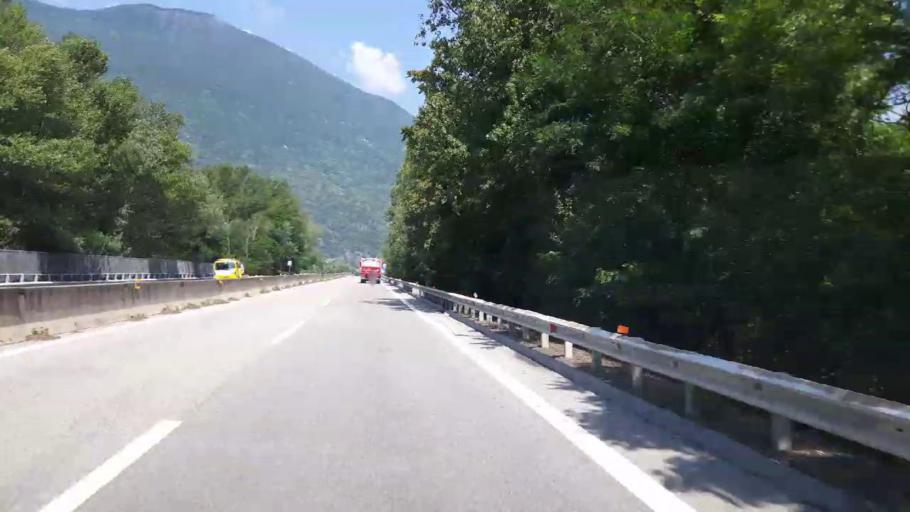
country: IT
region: Piedmont
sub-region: Provincia Verbano-Cusio-Ossola
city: Pallanzeno
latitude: 46.0351
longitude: 8.2731
